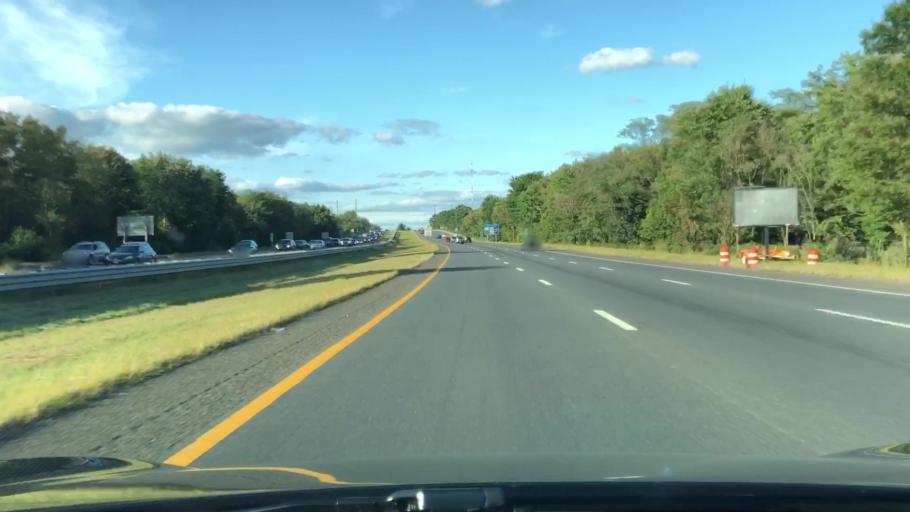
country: US
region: New Jersey
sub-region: Mercer County
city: Mercerville
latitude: 40.2572
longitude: -74.6940
